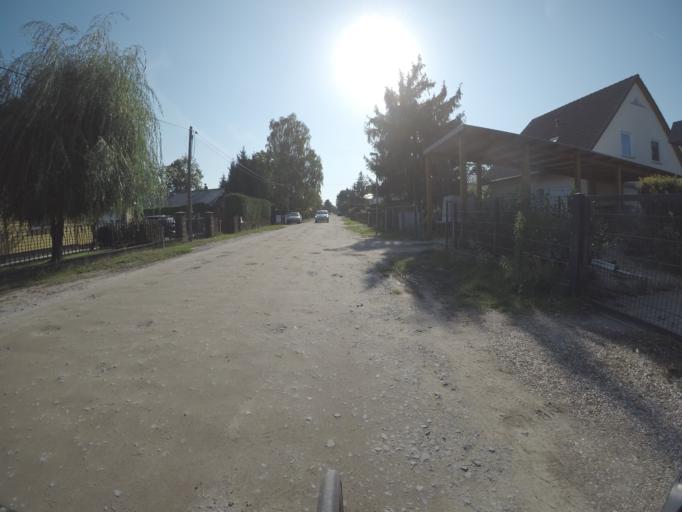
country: DE
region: Brandenburg
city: Oranienburg
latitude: 52.7250
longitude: 13.2353
